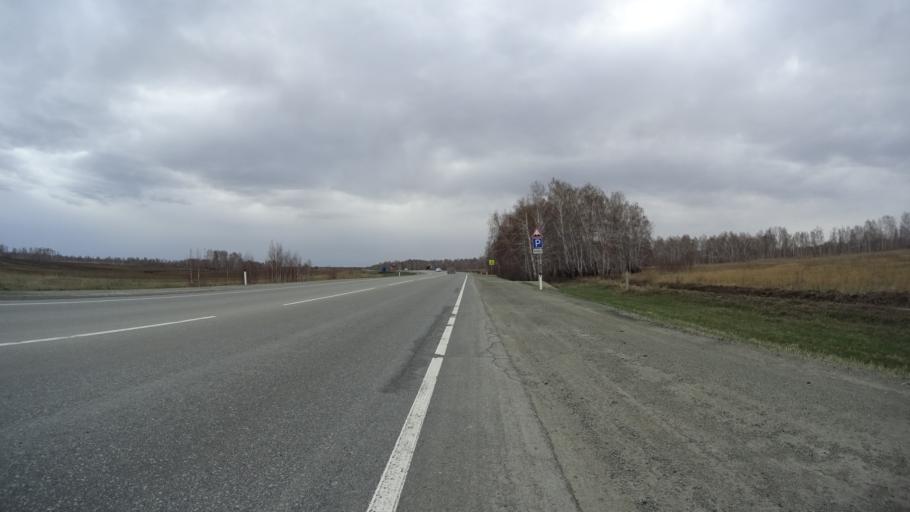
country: RU
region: Chelyabinsk
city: Yemanzhelinsk
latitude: 54.6986
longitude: 61.2511
